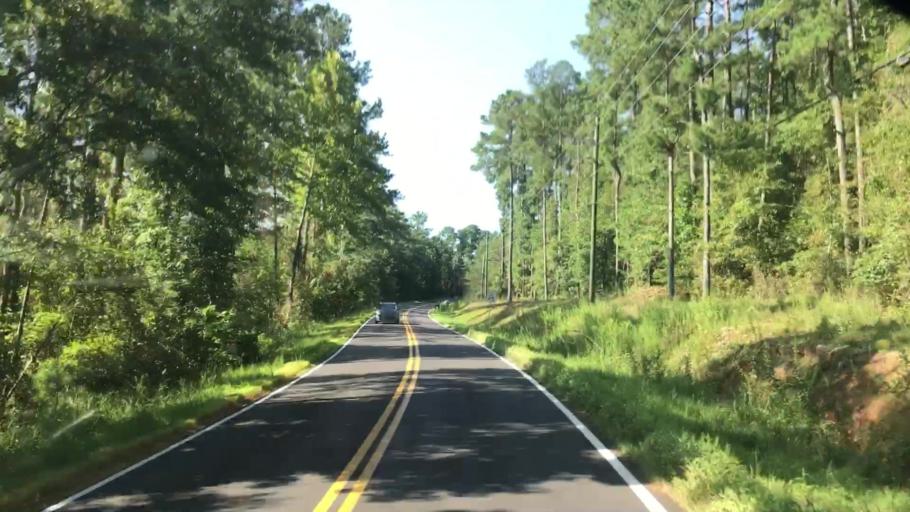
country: US
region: Georgia
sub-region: Walton County
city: Monroe
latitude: 33.8372
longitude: -83.7908
